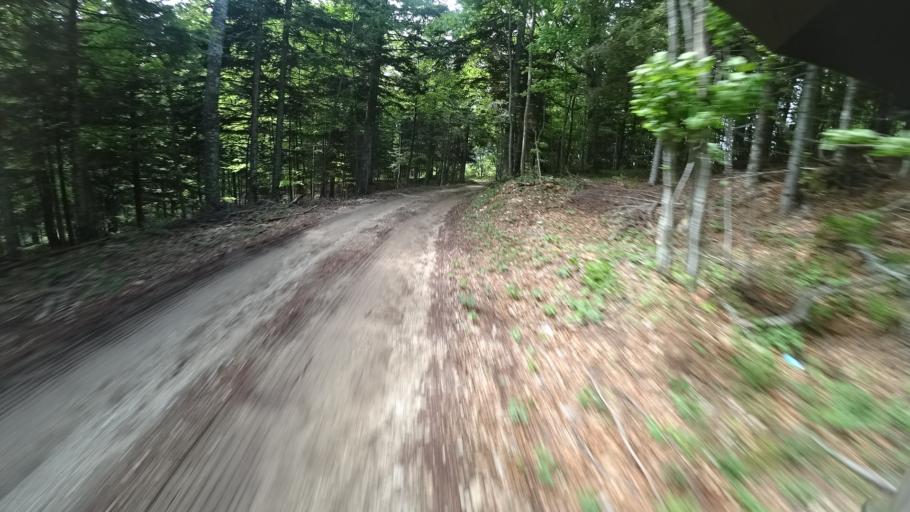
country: BA
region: Federation of Bosnia and Herzegovina
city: Bihac
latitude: 44.6805
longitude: 15.8444
